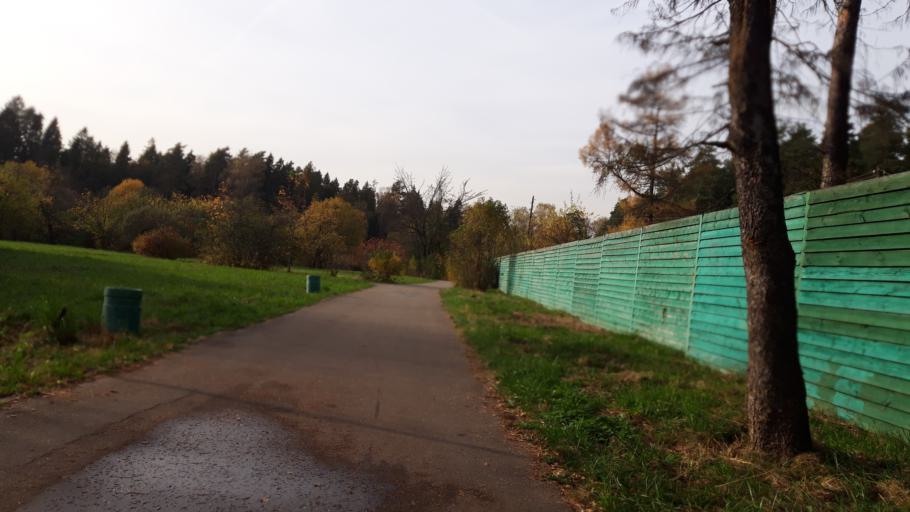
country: RU
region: Moscow
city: Zelenograd
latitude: 56.0002
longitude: 37.1827
